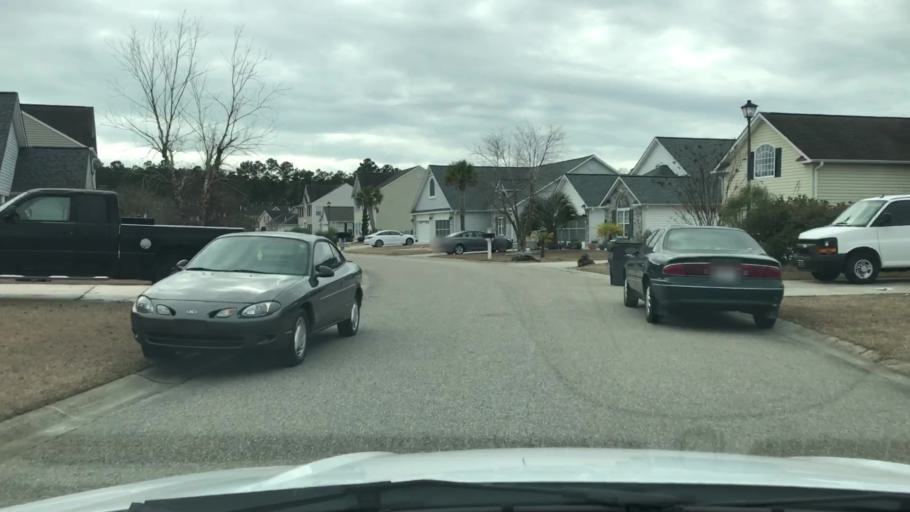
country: US
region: South Carolina
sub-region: Horry County
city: Socastee
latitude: 33.6715
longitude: -78.9735
